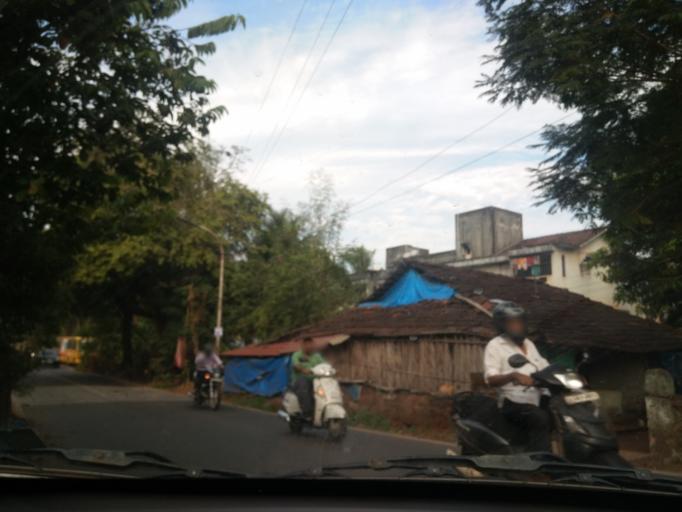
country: IN
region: Goa
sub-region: South Goa
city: Raia
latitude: 15.2914
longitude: 73.9752
